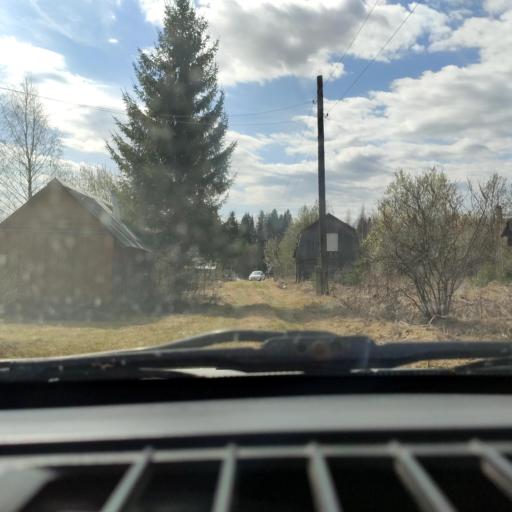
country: RU
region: Perm
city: Kultayevo
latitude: 57.8260
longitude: 55.7747
